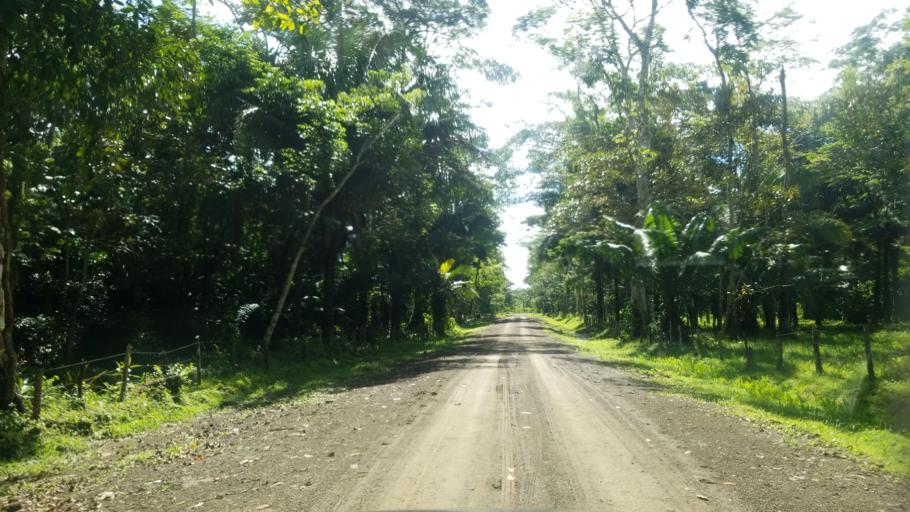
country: CR
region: Alajuela
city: San Jose
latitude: 11.0853
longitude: -85.2586
